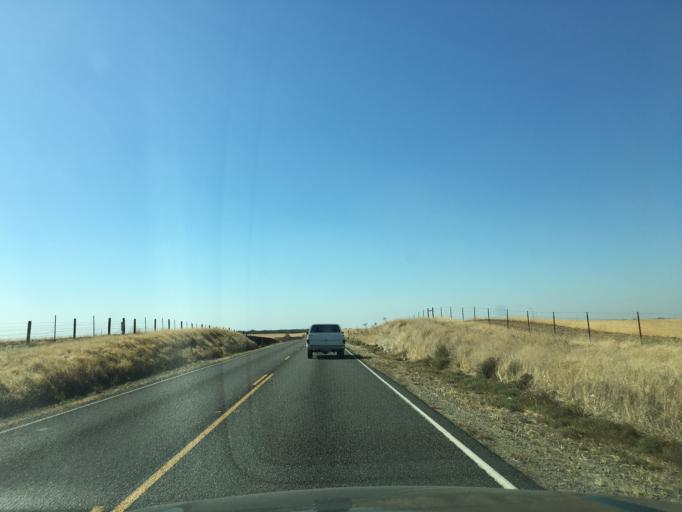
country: US
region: California
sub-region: Madera County
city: Bonadelle Ranchos-Madera Ranchos
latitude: 37.0102
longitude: -119.9133
